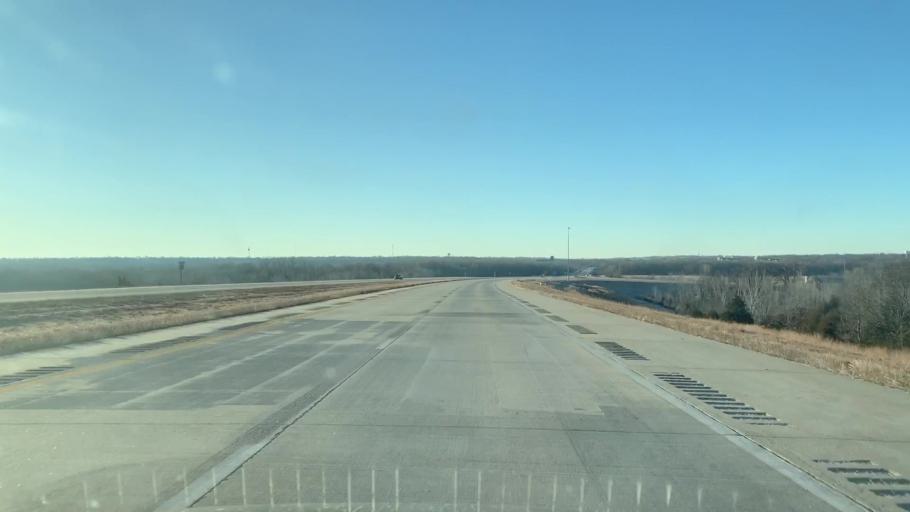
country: US
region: Kansas
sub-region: Bourbon County
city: Fort Scott
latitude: 37.8621
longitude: -94.7032
